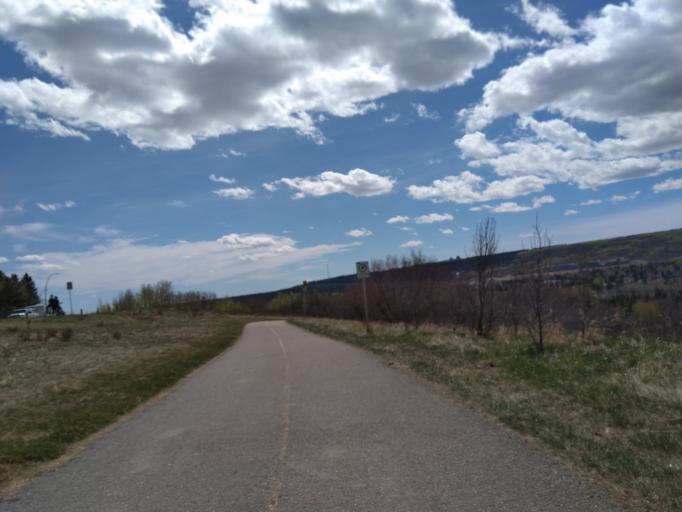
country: CA
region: Alberta
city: Calgary
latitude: 51.0998
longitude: -114.1905
